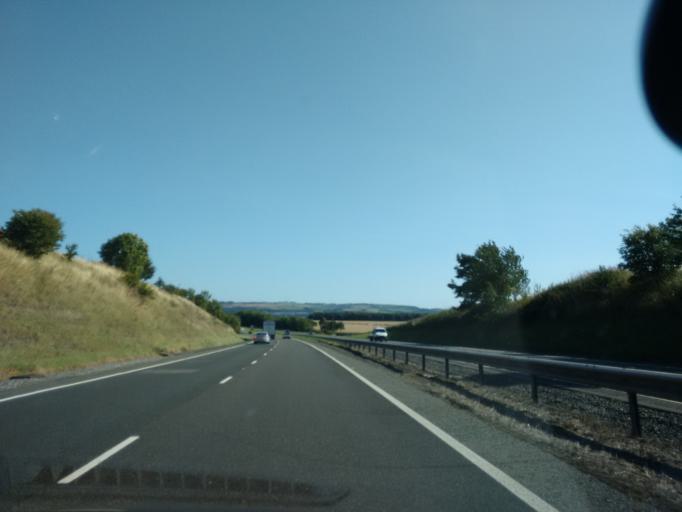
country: GB
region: England
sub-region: Northumberland
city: Corbridge
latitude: 54.9699
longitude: -1.9761
